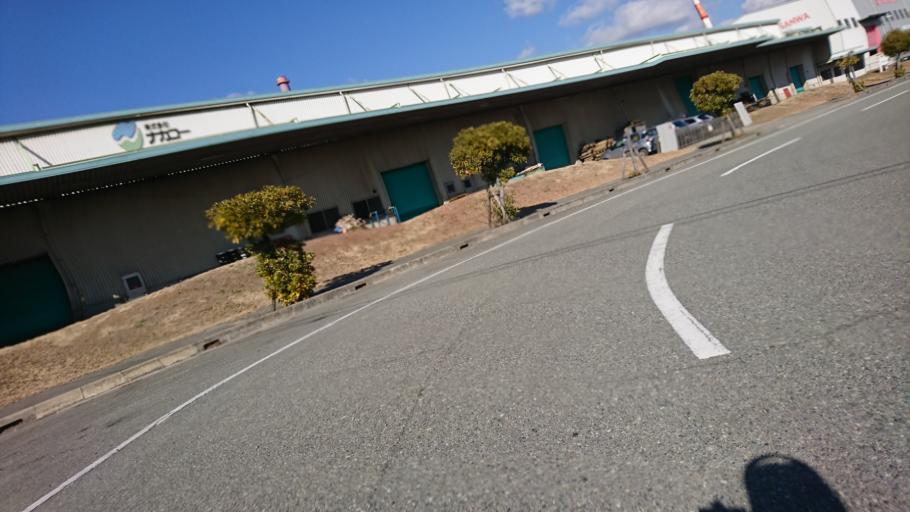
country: JP
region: Hyogo
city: Kakogawacho-honmachi
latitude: 34.7528
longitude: 134.7810
